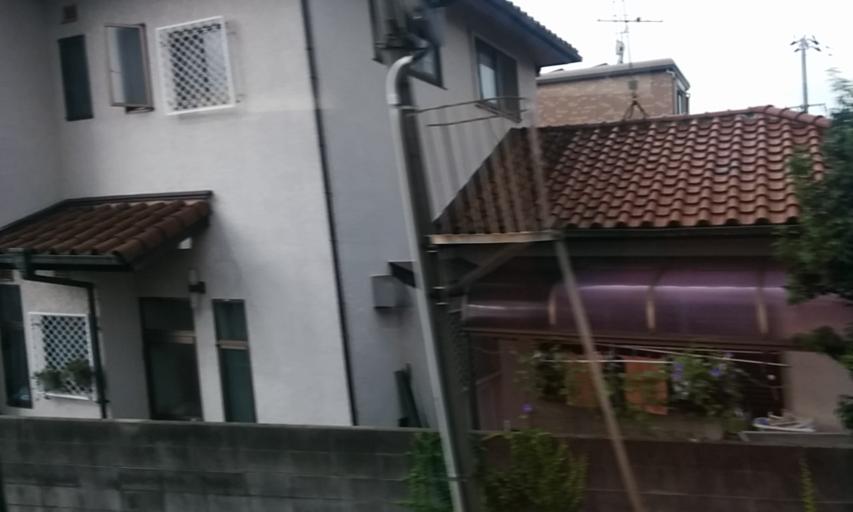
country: JP
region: Nara
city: Tawaramoto
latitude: 34.5553
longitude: 135.7901
